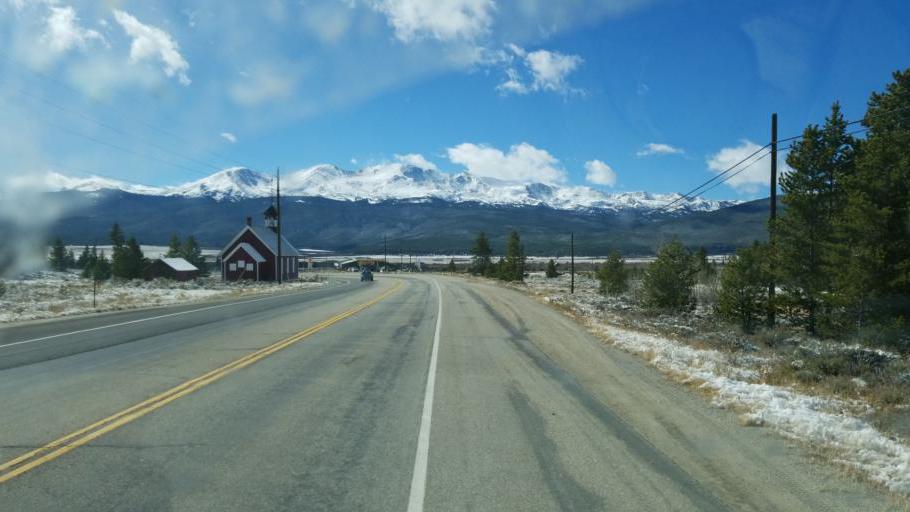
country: US
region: Colorado
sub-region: Lake County
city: Leadville North
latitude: 39.2248
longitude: -106.3452
